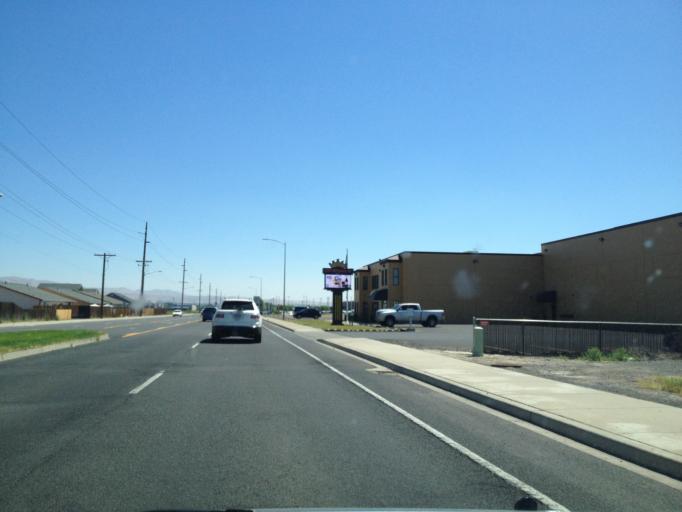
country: US
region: Washington
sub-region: Yakima County
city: Union Gap
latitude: 46.5634
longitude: -120.5071
